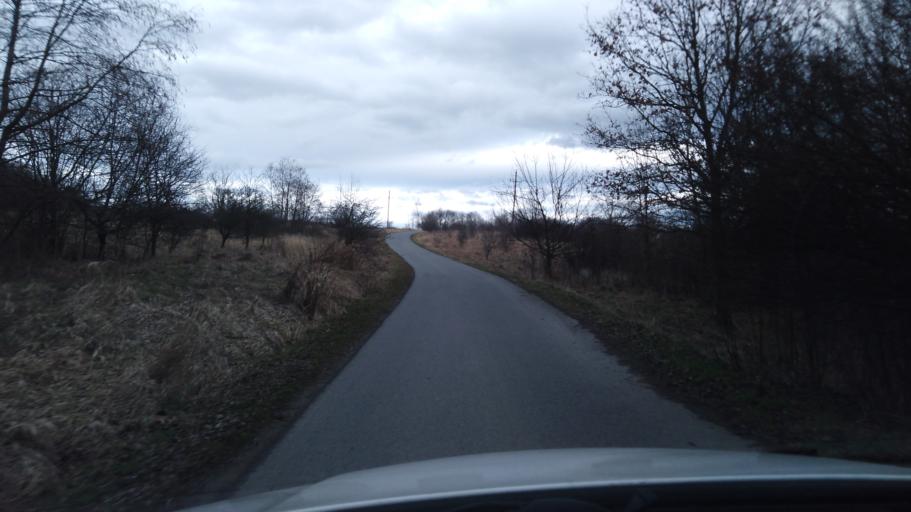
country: PL
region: Silesian Voivodeship
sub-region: Powiat zywiecki
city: Trzebinia
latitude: 49.6580
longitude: 19.2060
